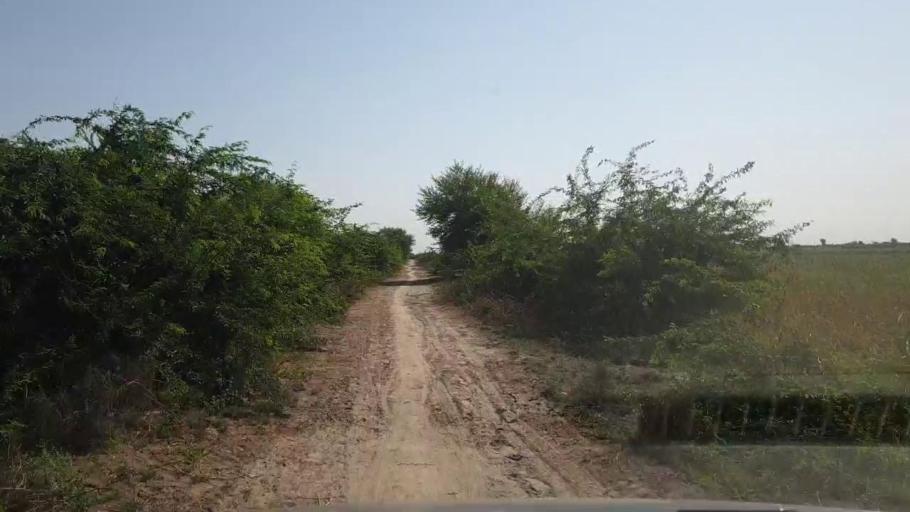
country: PK
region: Sindh
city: Kadhan
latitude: 24.5978
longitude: 69.0052
